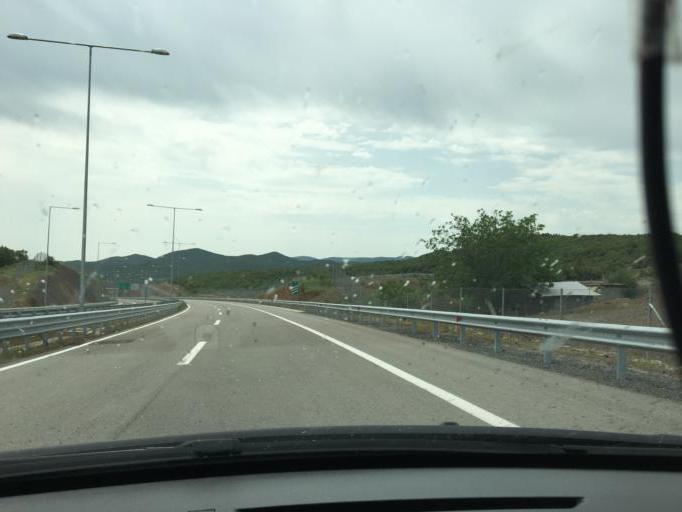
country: MK
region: Gevgelija
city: Miravci
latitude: 41.3017
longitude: 22.4280
